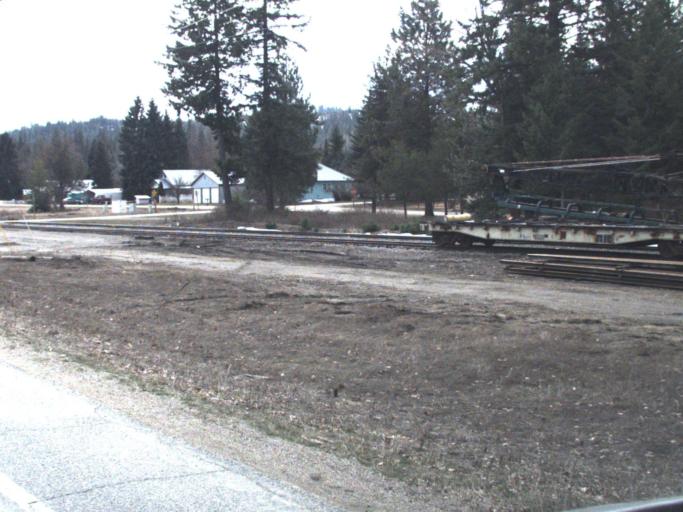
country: US
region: Washington
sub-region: Pend Oreille County
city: Newport
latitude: 48.2482
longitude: -117.2394
